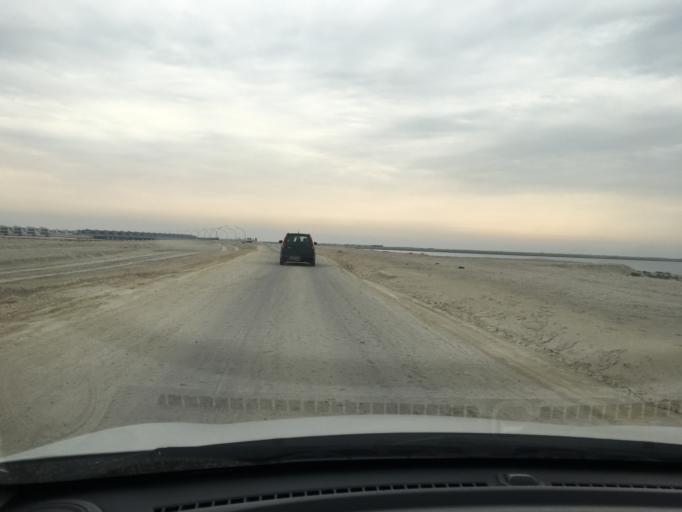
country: BH
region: Central Governorate
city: Dar Kulayb
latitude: 25.8307
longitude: 50.5954
